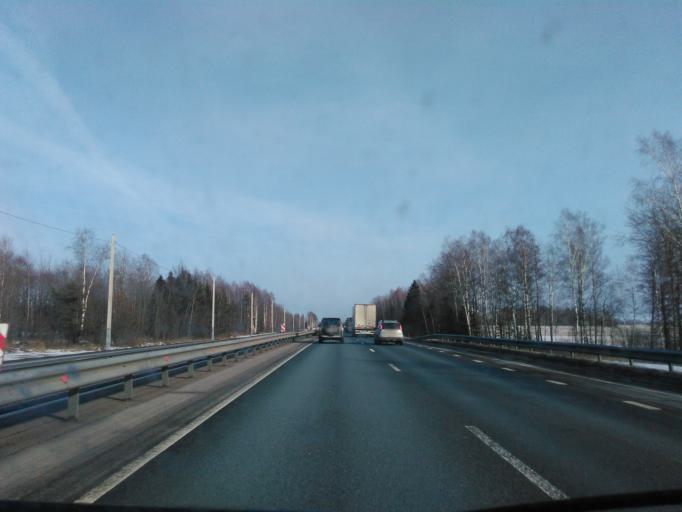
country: RU
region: Smolensk
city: Verkhnedneprovskiy
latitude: 55.1820
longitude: 33.5520
